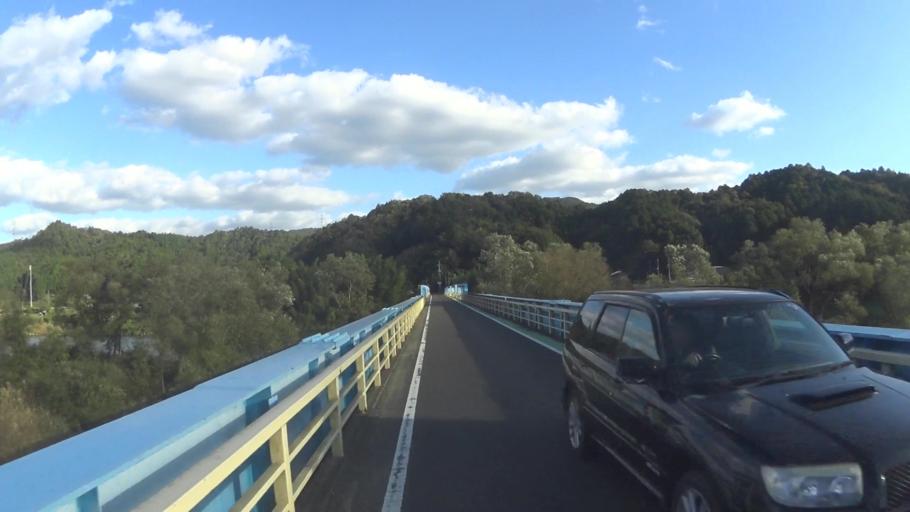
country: JP
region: Kyoto
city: Maizuru
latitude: 35.4292
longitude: 135.2537
